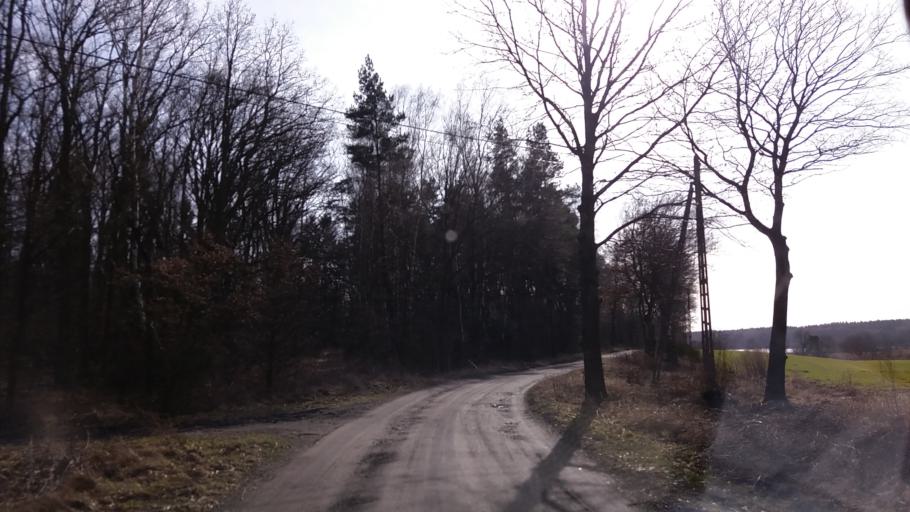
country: PL
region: West Pomeranian Voivodeship
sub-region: Powiat choszczenski
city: Pelczyce
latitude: 53.0022
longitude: 15.3696
